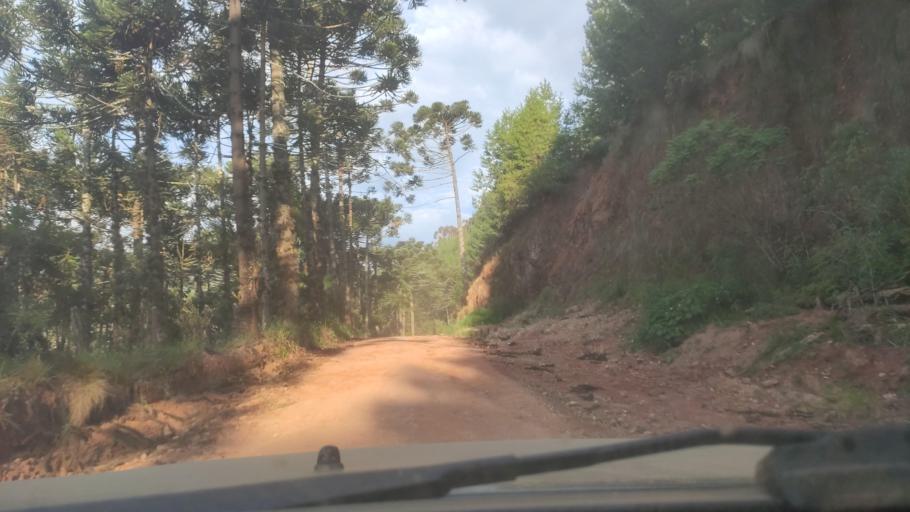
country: BR
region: Minas Gerais
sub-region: Cambui
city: Cambui
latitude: -22.7380
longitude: -45.9090
